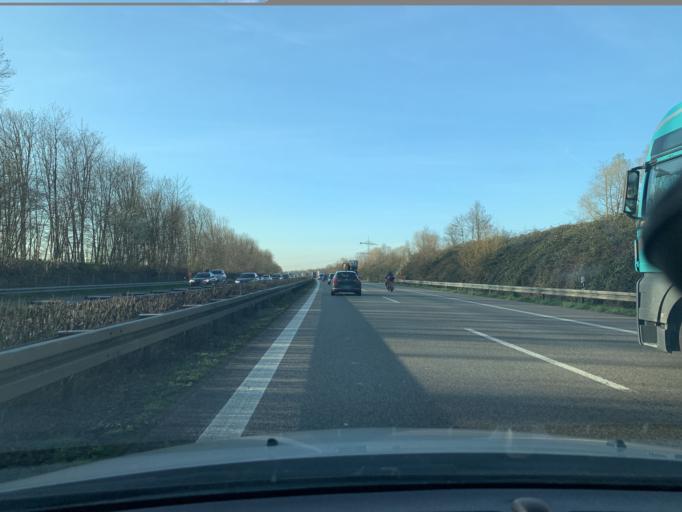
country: DE
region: Baden-Wuerttemberg
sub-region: Freiburg Region
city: Vorstetten
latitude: 48.0744
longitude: 7.8082
